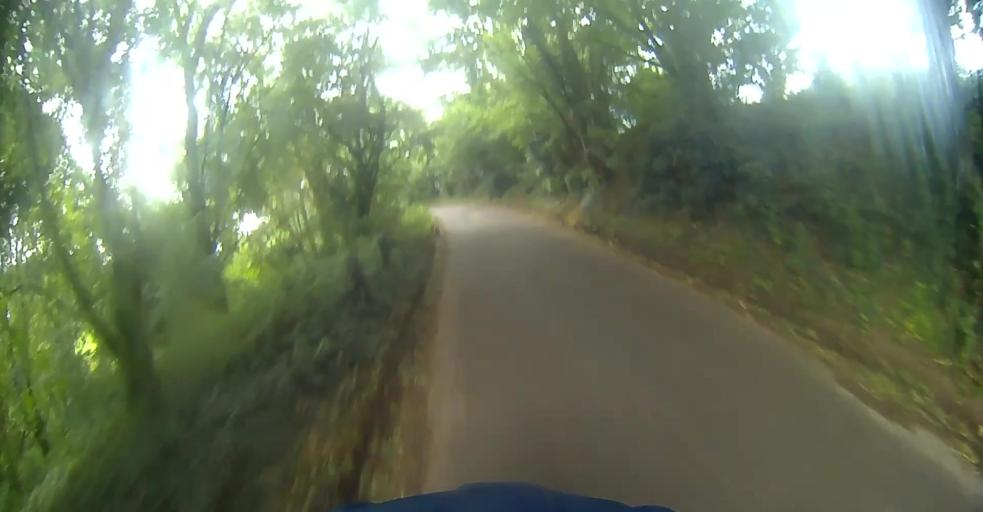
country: GB
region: England
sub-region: Hampshire
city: Alton
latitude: 51.1818
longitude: -1.0246
